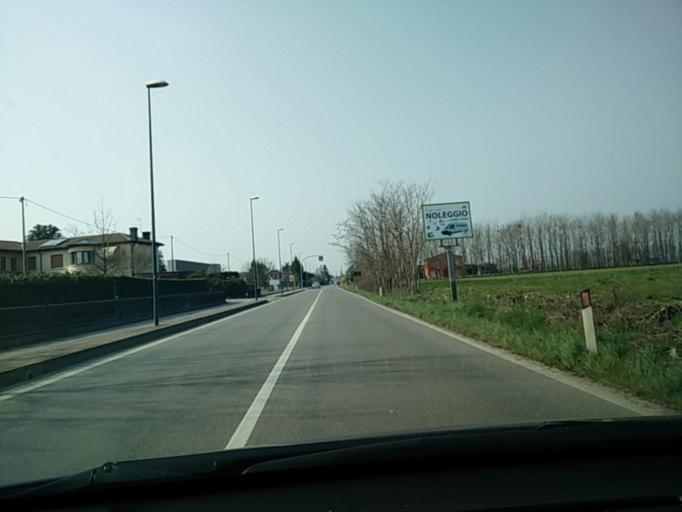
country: IT
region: Veneto
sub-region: Provincia di Treviso
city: Postioma
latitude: 45.7108
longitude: 12.1651
